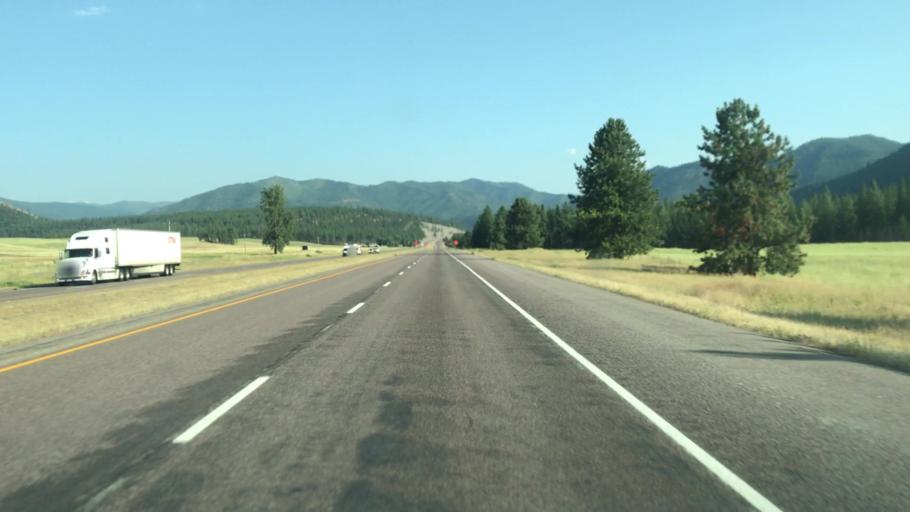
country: US
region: Montana
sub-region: Mineral County
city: Superior
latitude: 47.0399
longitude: -114.7488
